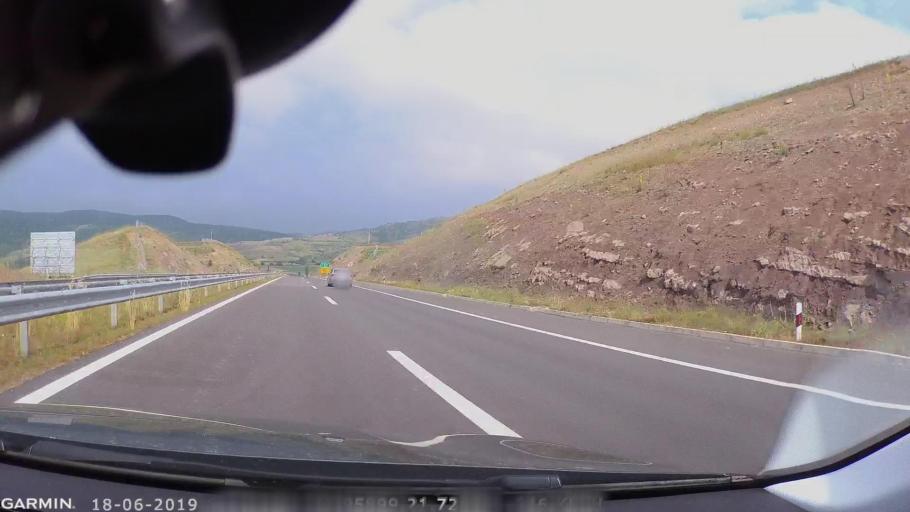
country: MK
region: Sveti Nikole
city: Gorobinci
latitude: 41.9324
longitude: 21.8266
